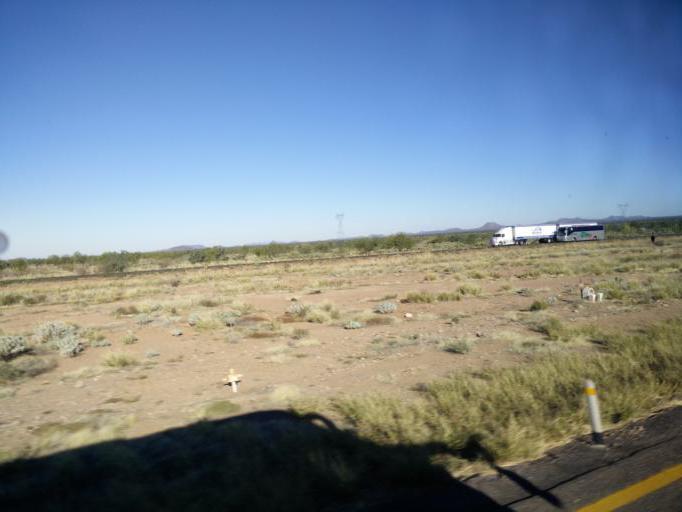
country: MX
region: Sonora
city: Hermosillo
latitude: 28.6113
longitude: -111.0170
